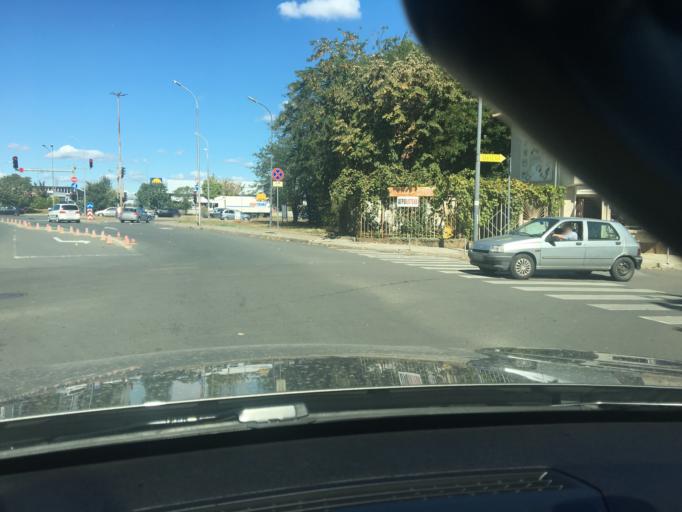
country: BG
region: Burgas
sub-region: Obshtina Burgas
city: Burgas
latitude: 42.5303
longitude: 27.4630
